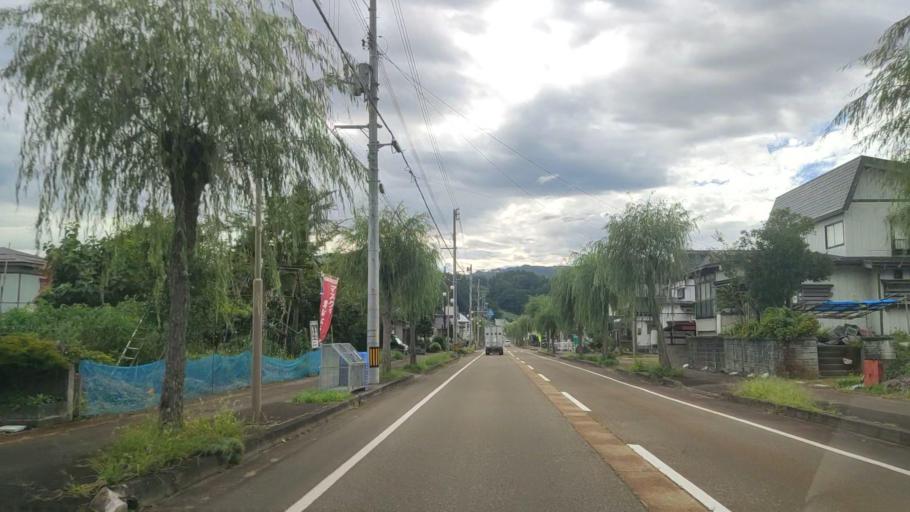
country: JP
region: Niigata
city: Arai
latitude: 37.0165
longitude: 138.2488
